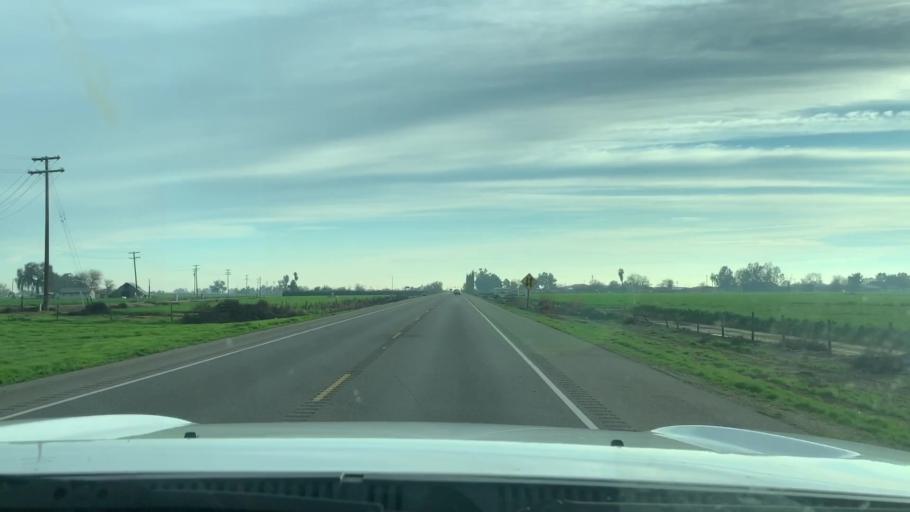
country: US
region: California
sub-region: Fresno County
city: Riverdale
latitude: 36.4425
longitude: -119.7989
